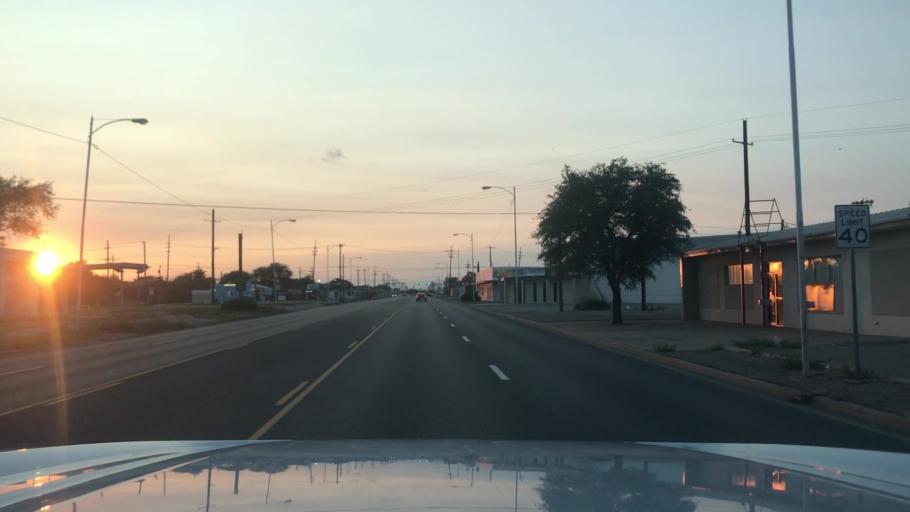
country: US
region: Texas
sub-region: Lubbock County
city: Lubbock
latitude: 33.5973
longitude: -101.8587
